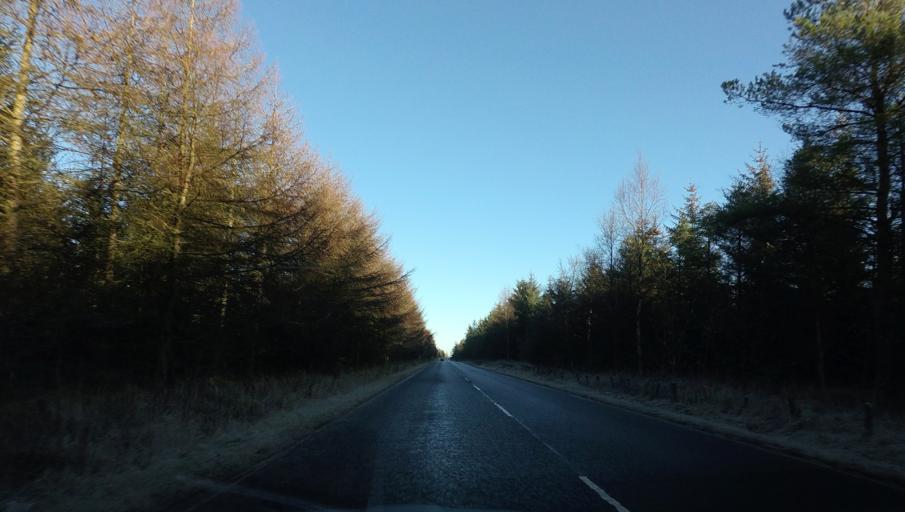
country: GB
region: Scotland
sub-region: West Lothian
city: Fauldhouse
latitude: 55.8156
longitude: -3.7005
